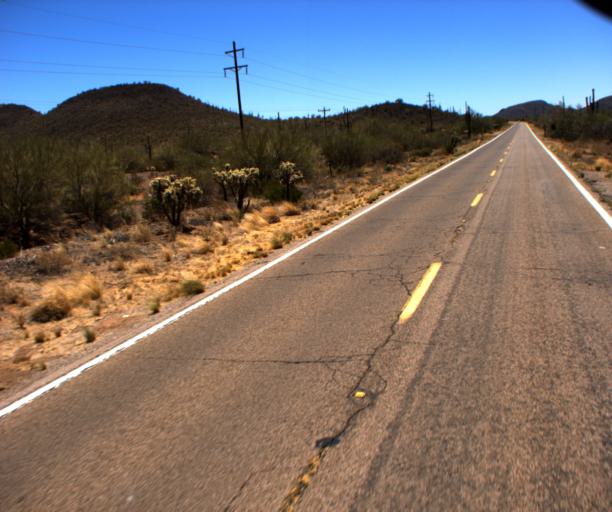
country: US
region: Arizona
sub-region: Pima County
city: Sells
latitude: 31.9890
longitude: -111.9764
